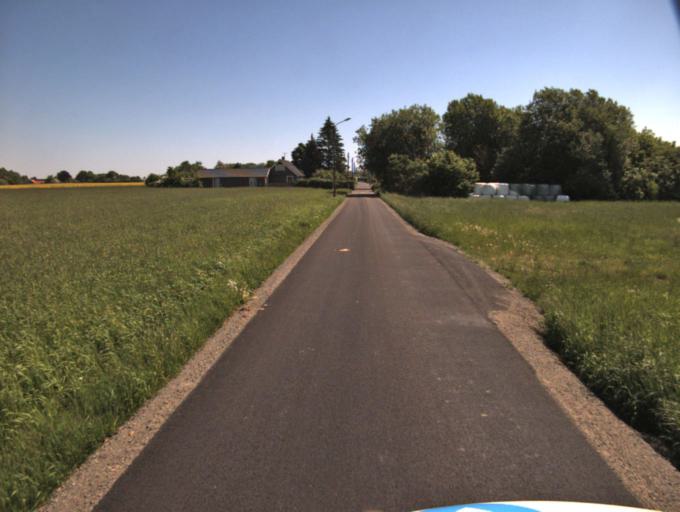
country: SE
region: Skane
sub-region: Kristianstads Kommun
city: Kristianstad
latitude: 56.0153
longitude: 14.2130
